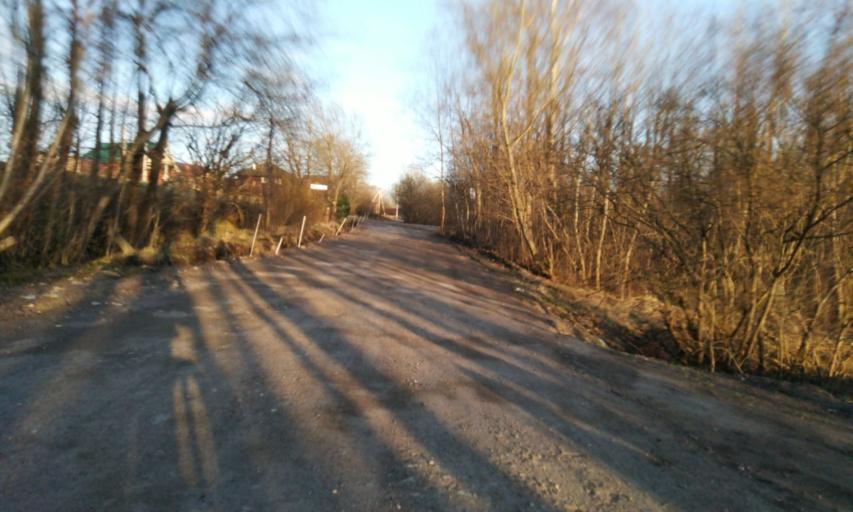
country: RU
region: Leningrad
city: Novoye Devyatkino
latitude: 60.0928
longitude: 30.4554
